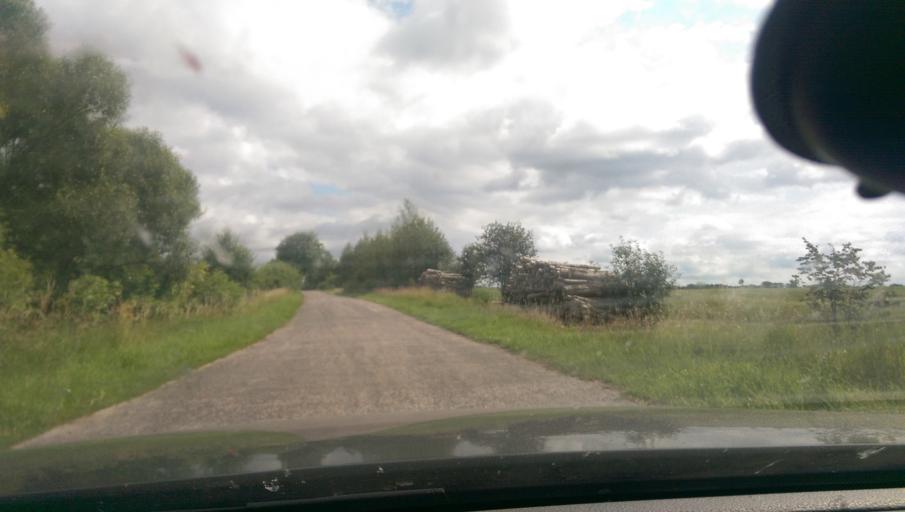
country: PL
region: Warmian-Masurian Voivodeship
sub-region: Powiat goldapski
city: Banie Mazurskie
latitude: 54.2241
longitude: 22.1801
